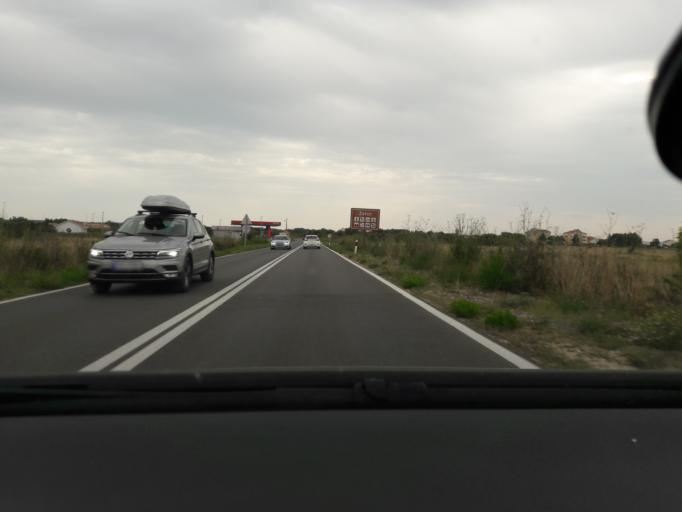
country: HR
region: Zadarska
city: Nin
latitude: 44.2284
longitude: 15.1797
